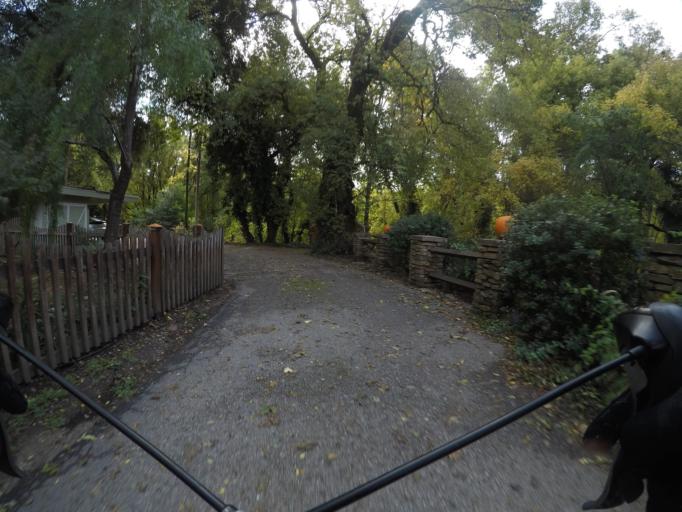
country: US
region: California
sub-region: Santa Cruz County
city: Ben Lomond
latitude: 37.0821
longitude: -122.0798
